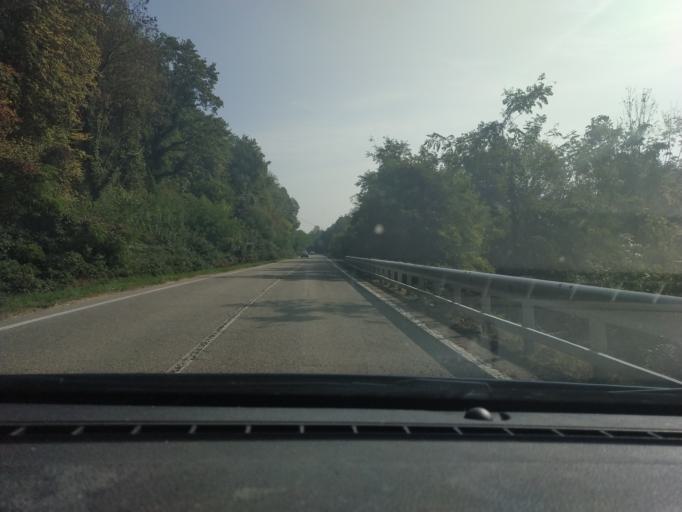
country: IT
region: Piedmont
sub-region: Provincia di Biella
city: Sala Biellese
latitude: 45.5176
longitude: 7.9764
